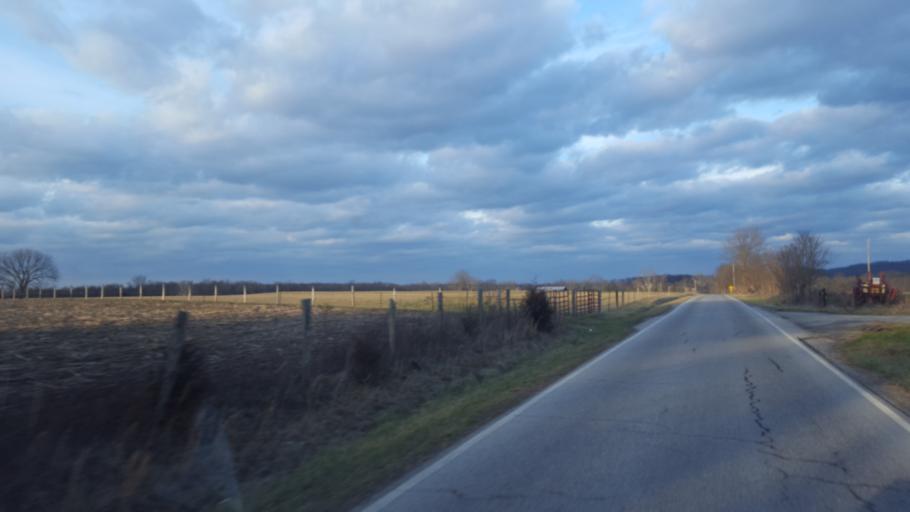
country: US
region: Kentucky
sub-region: Fleming County
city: Flemingsburg
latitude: 38.4835
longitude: -83.5992
